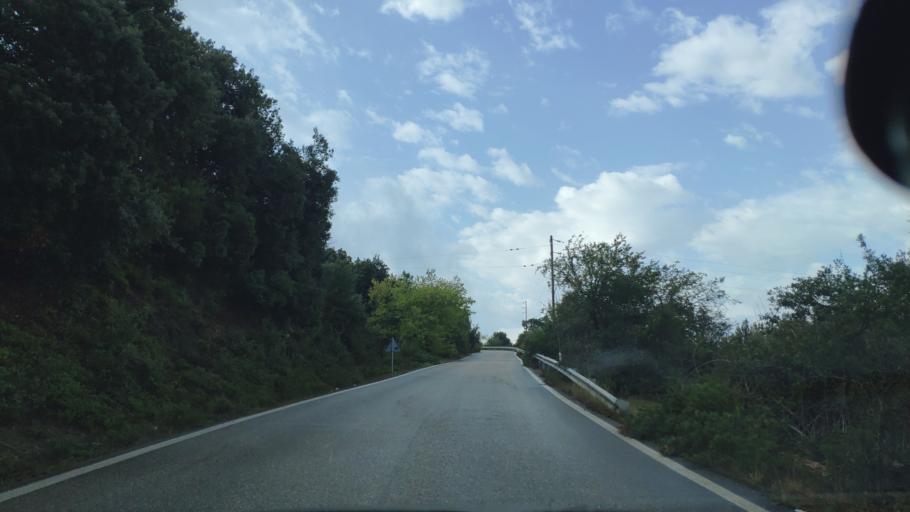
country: GR
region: West Greece
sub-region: Nomos Aitolias kai Akarnanias
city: Sardinia
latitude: 38.8787
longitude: 21.2659
